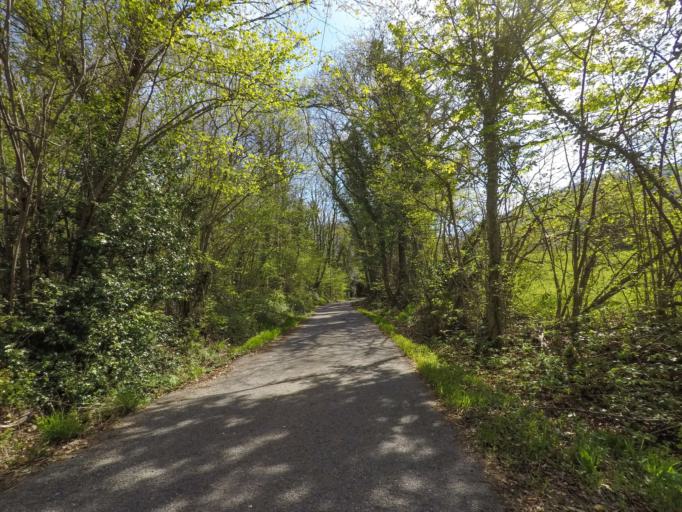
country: FR
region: Rhone-Alpes
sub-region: Departement de la Haute-Savoie
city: Collonges-sous-Saleve
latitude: 46.1271
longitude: 6.1530
